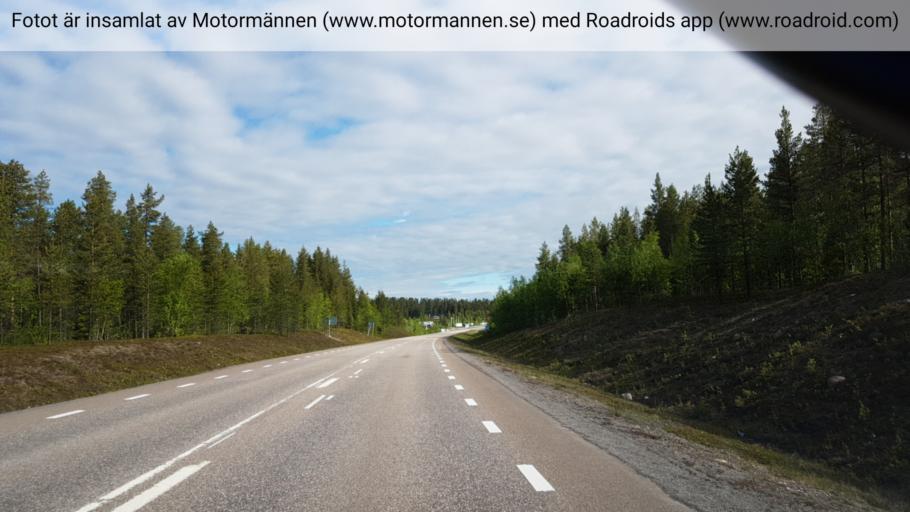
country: SE
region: Norrbotten
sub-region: Gallivare Kommun
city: Malmberget
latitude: 67.4853
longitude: 21.1214
